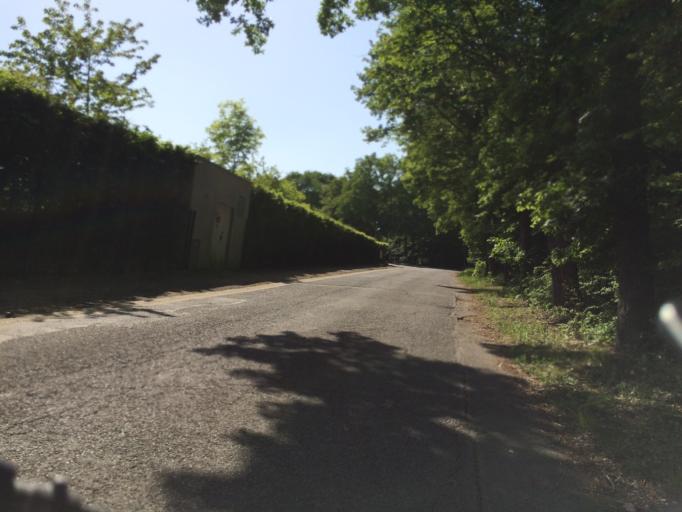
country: FR
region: Ile-de-France
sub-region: Departement de l'Essonne
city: Verrieres-le-Buisson
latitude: 48.7484
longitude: 2.2507
